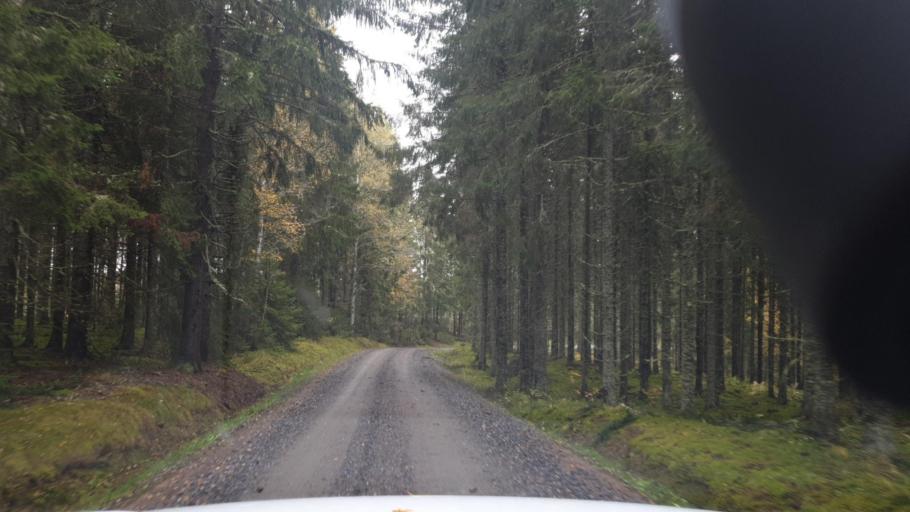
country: SE
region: Vaermland
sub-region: Karlstads Kommun
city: Edsvalla
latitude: 59.4620
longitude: 13.1062
